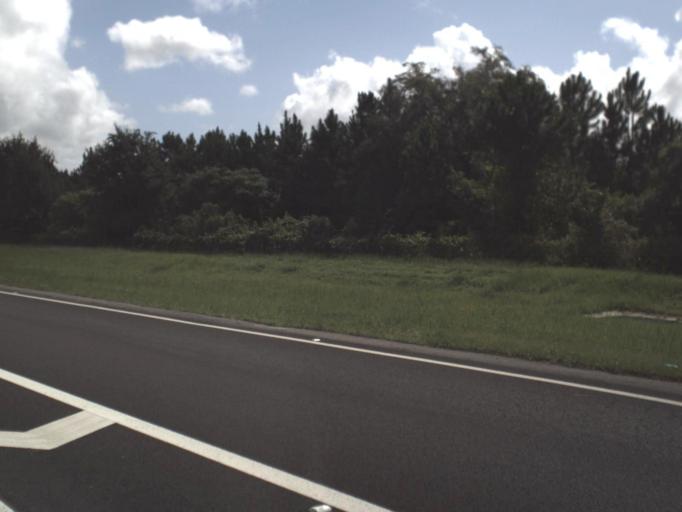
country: US
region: Florida
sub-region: Pasco County
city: Wesley Chapel
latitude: 28.2425
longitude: -82.3500
